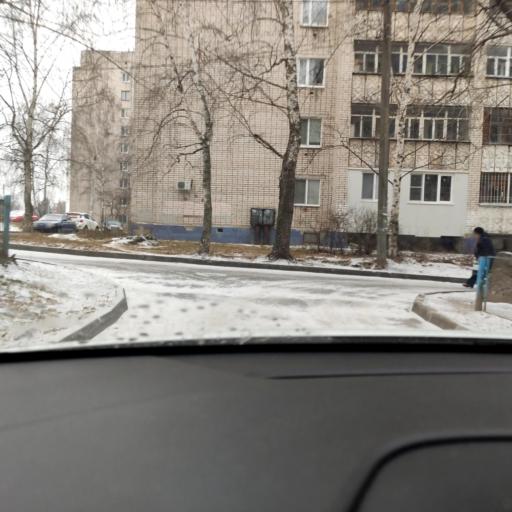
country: RU
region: Tatarstan
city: Vysokaya Gora
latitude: 55.8591
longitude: 49.2310
